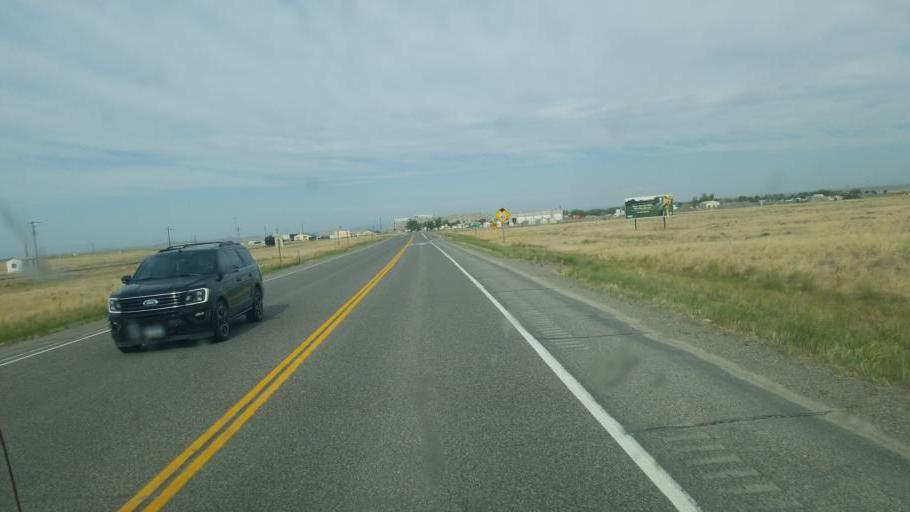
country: US
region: Wyoming
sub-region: Fremont County
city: Riverton
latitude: 43.2365
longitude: -108.0936
